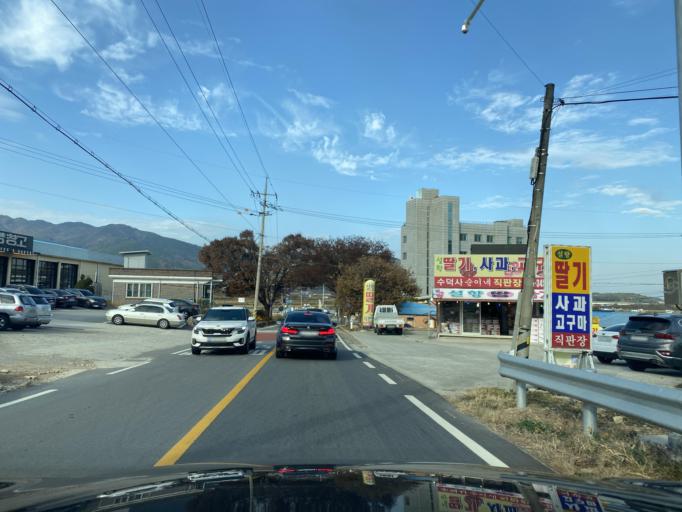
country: KR
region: Chungcheongnam-do
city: Hongsung
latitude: 36.6738
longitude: 126.6425
